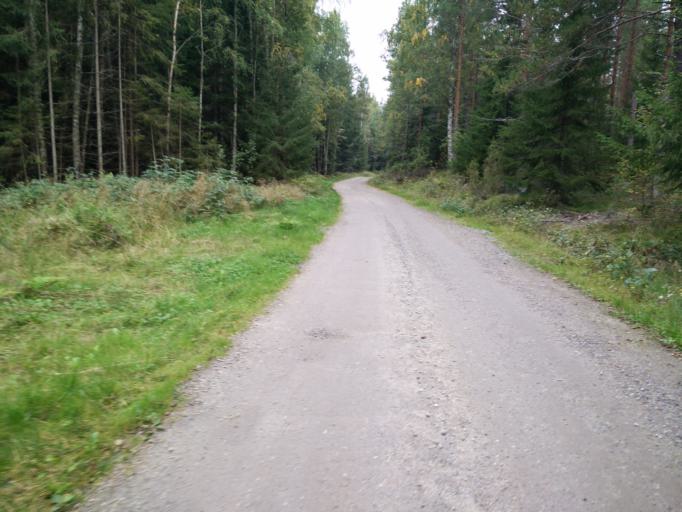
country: SE
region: Gaevleborg
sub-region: Hudiksvalls Kommun
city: Hudiksvall
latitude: 61.8327
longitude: 17.3361
